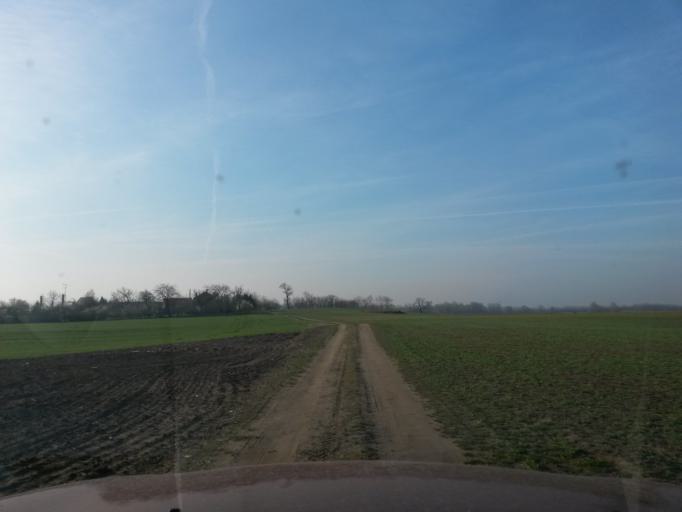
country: SK
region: Nitriansky
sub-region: Okres Komarno
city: Hurbanovo
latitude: 47.8860
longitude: 18.1712
